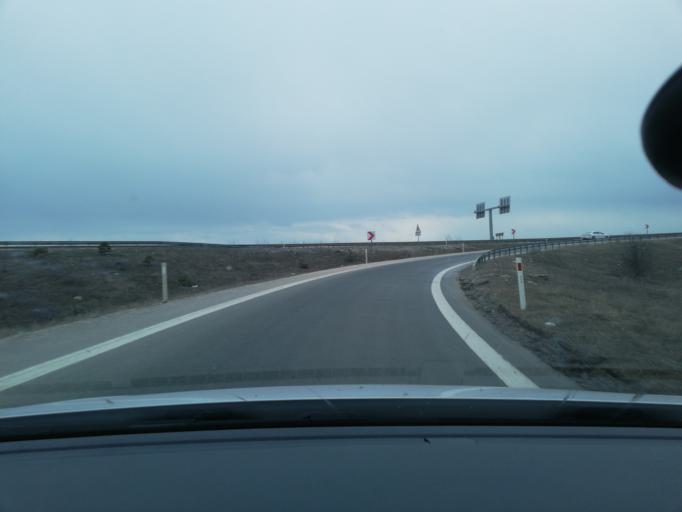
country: TR
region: Bolu
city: Gerede
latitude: 40.7770
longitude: 32.2174
